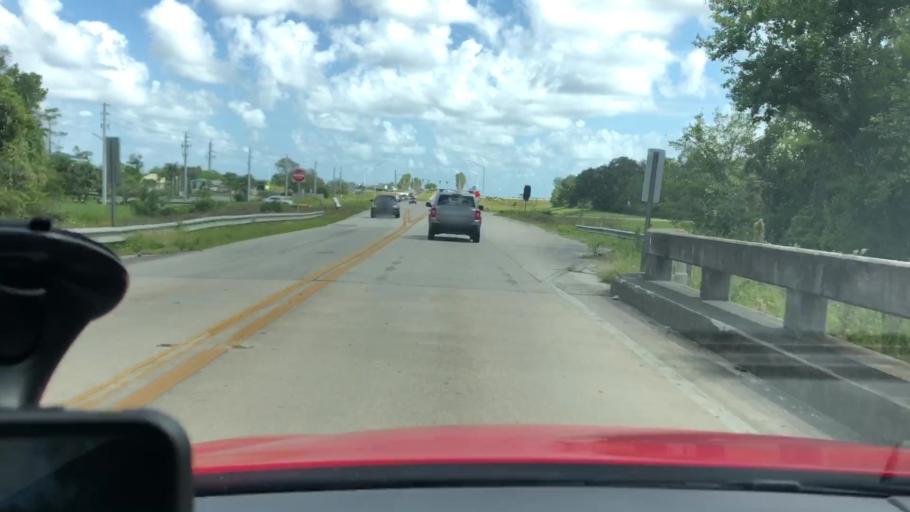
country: US
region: Florida
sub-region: Volusia County
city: Holly Hill
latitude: 29.2173
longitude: -81.1092
